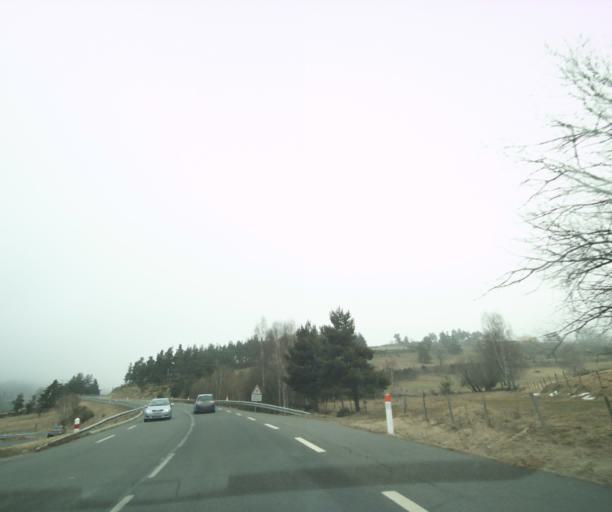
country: FR
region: Languedoc-Roussillon
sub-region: Departement de la Lozere
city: Langogne
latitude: 44.6711
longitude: 3.7643
